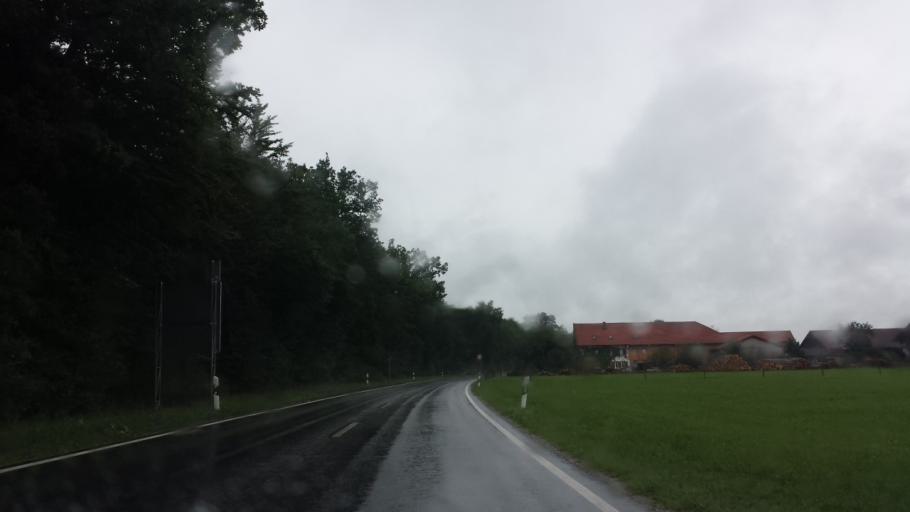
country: DE
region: Bavaria
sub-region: Upper Bavaria
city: Aying
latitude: 47.9369
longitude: 11.7568
